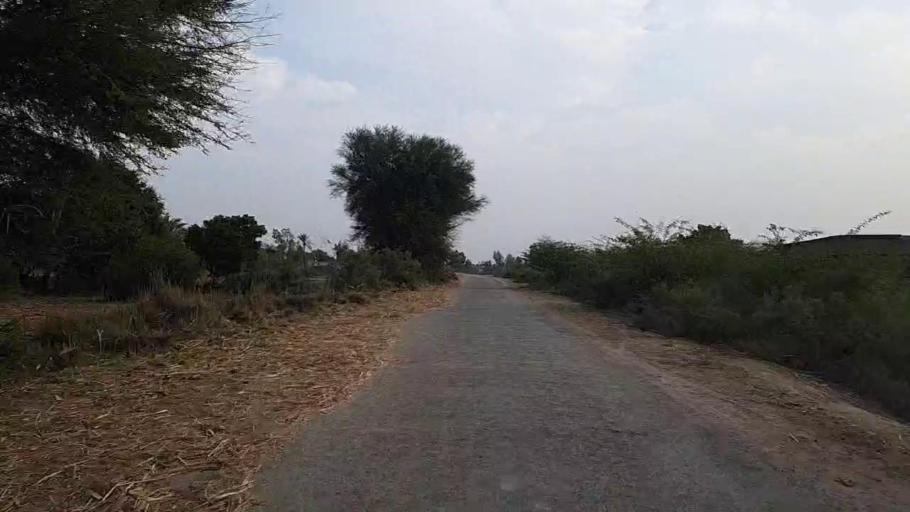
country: PK
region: Sindh
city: Pithoro
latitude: 25.4610
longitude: 69.2765
